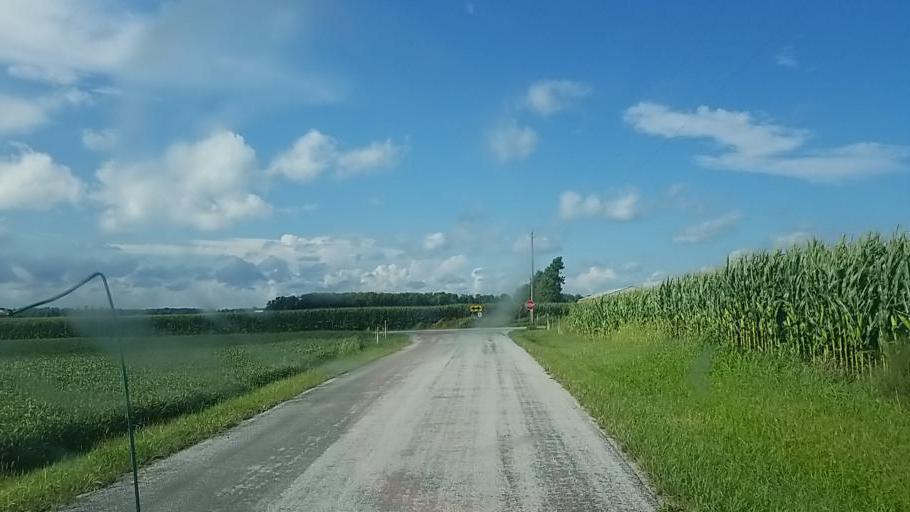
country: US
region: Ohio
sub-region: Hardin County
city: Kenton
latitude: 40.7014
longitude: -83.5309
